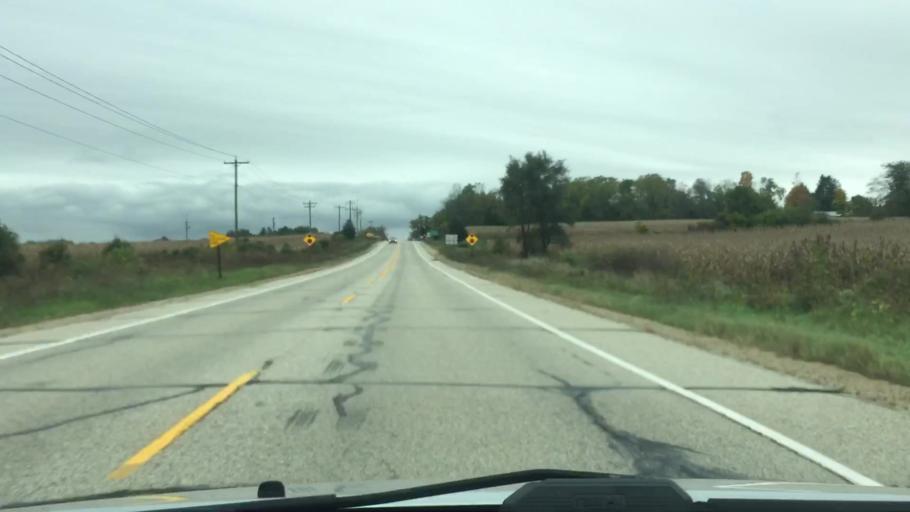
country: US
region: Wisconsin
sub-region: Jefferson County
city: Palmyra
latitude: 42.8034
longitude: -88.5627
